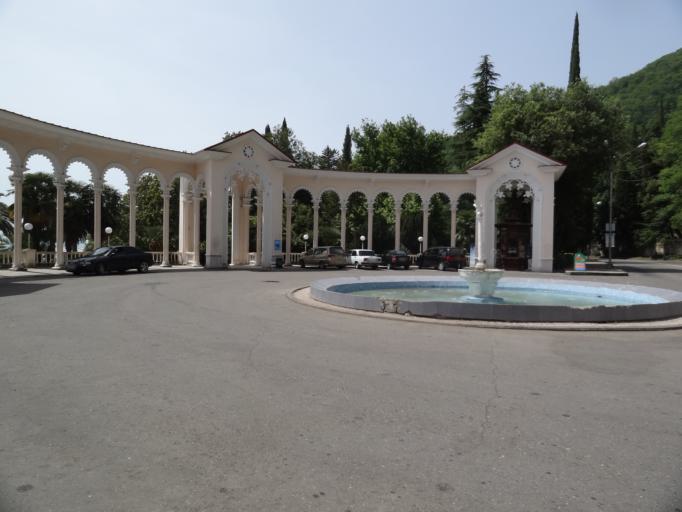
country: GE
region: Abkhazia
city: Gagra
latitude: 43.3215
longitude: 40.2371
